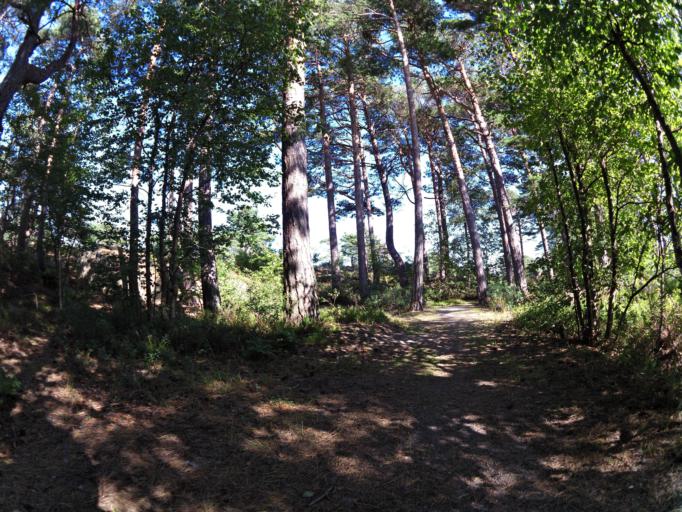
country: NO
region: Ostfold
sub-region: Fredrikstad
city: Fredrikstad
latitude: 59.1678
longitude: 10.8375
